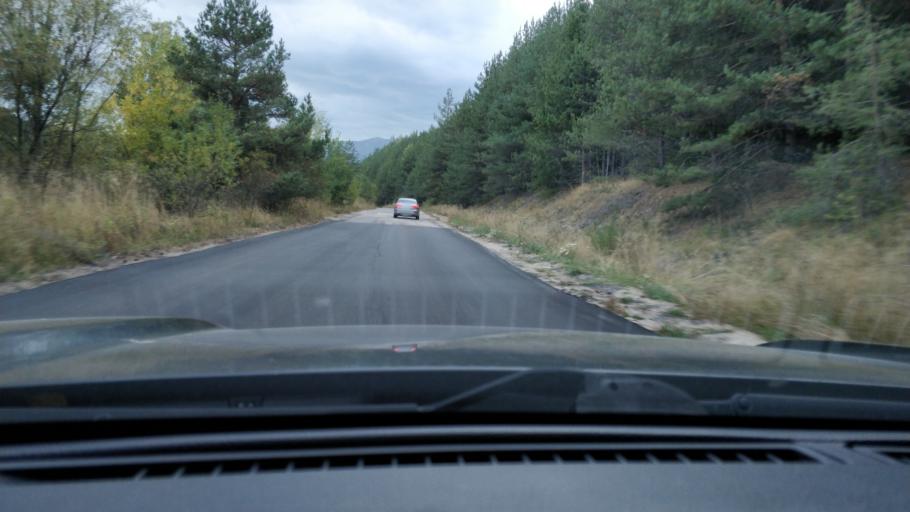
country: BG
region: Sofiya
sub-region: Obshtina Samokov
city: Samokov
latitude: 42.4817
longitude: 23.3928
